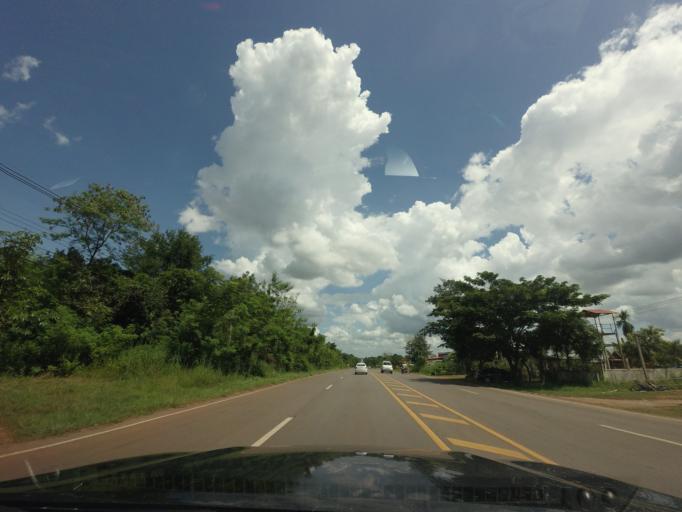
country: TH
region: Changwat Udon Thani
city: Ban Dung
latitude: 17.6841
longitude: 103.2129
